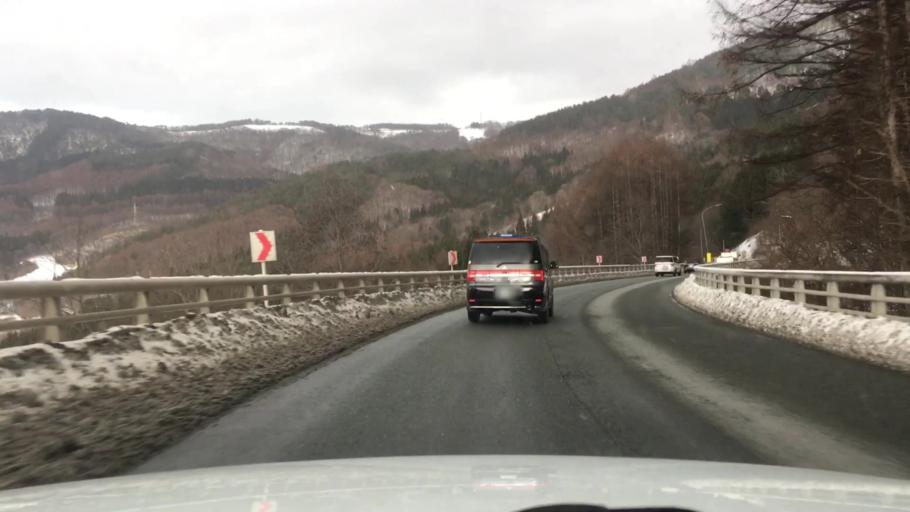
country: JP
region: Iwate
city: Morioka-shi
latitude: 39.6647
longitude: 141.3276
